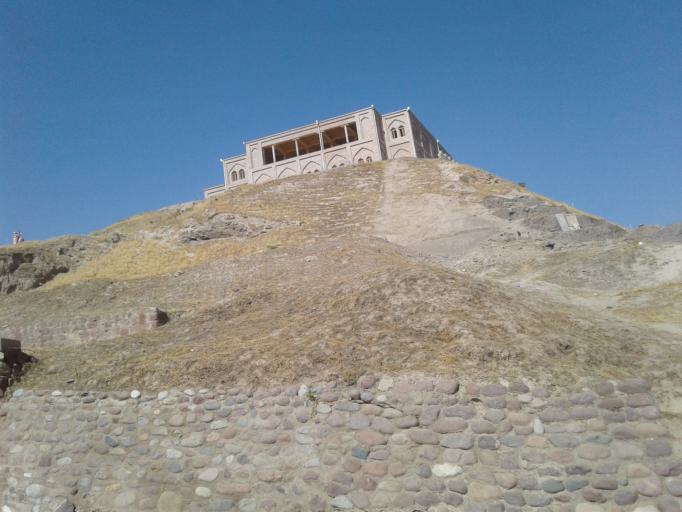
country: TJ
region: Republican Subordination
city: Hisor
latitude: 38.4838
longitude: 68.5935
